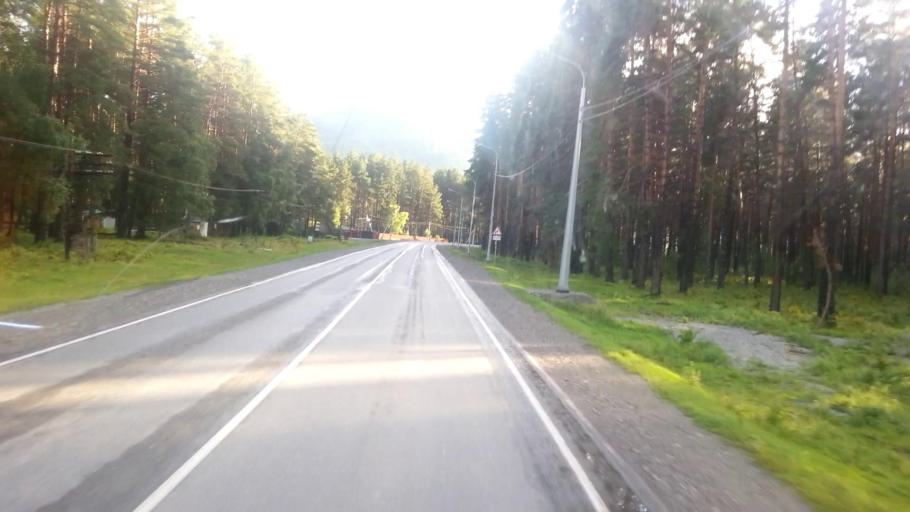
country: RU
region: Altay
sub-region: Mayminskiy Rayon
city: Manzherok
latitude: 51.8328
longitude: 85.7667
